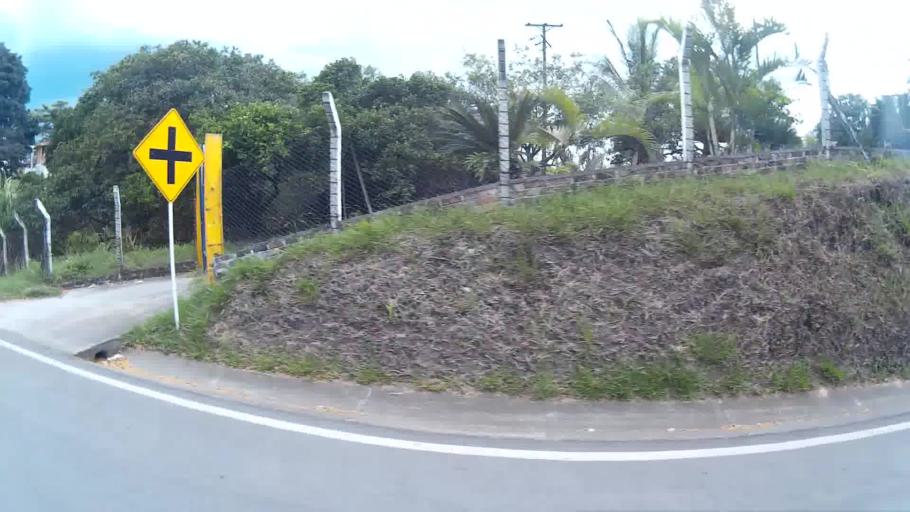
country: CO
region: Risaralda
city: Pereira
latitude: 4.8133
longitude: -75.7827
